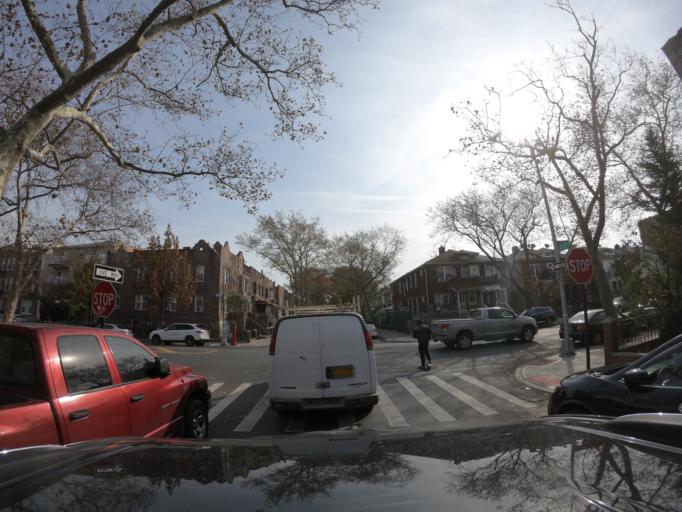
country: US
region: New York
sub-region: Kings County
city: Bensonhurst
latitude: 40.6143
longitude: -73.9776
